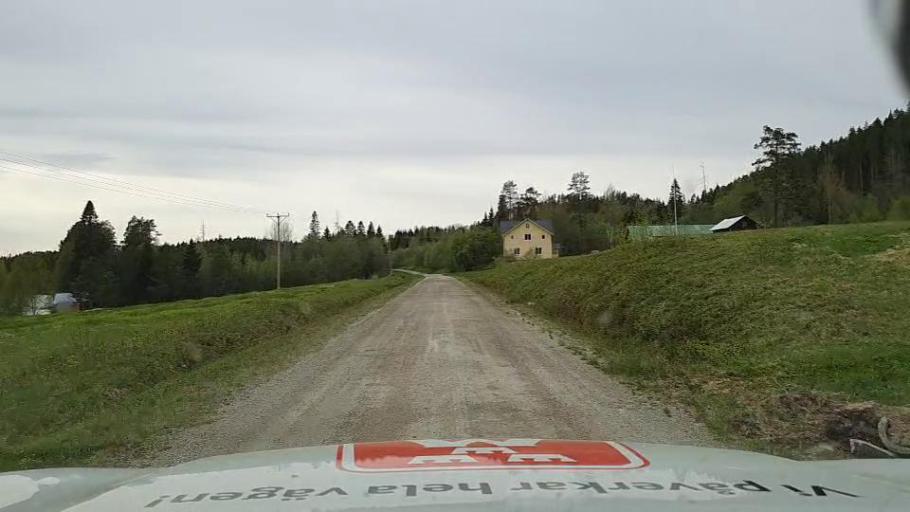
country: SE
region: Jaemtland
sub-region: Bergs Kommun
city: Hoverberg
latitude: 62.6670
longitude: 14.8180
